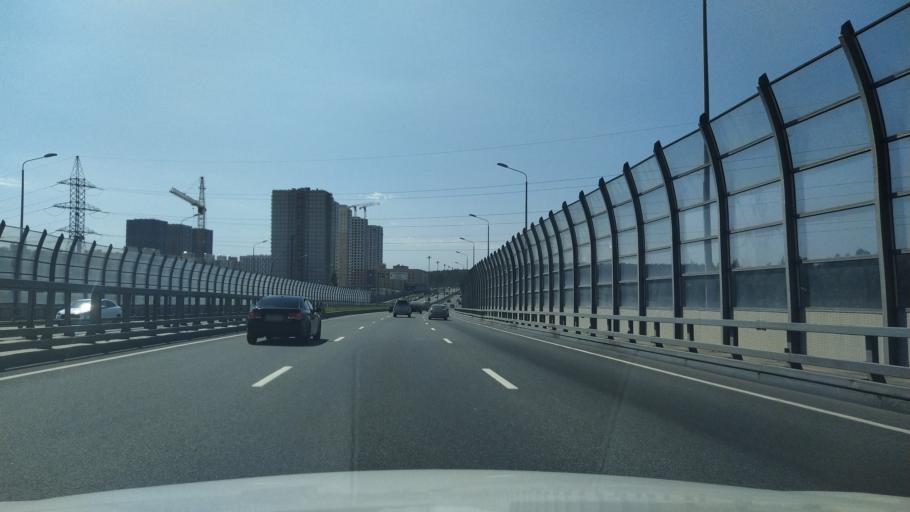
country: RU
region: St.-Petersburg
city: Shuvalovo
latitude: 60.0614
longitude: 30.2809
